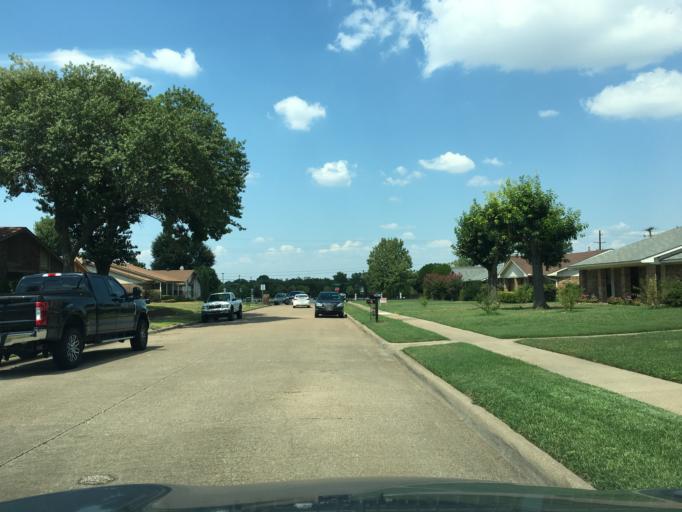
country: US
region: Texas
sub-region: Dallas County
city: Garland
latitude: 32.9502
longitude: -96.6613
